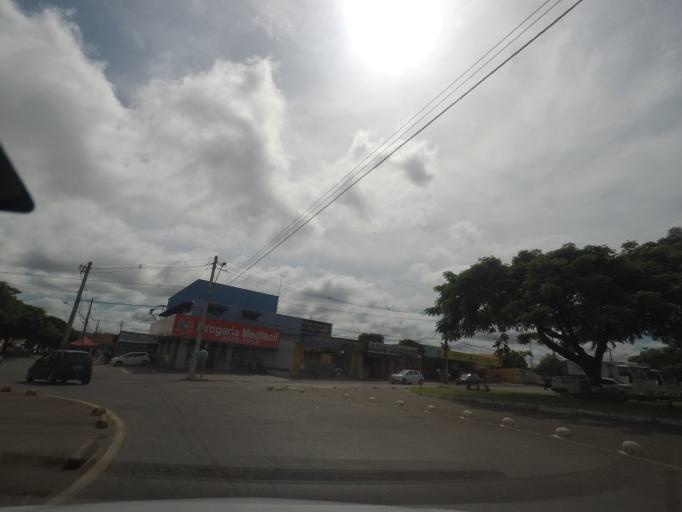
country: BR
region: Goias
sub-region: Goiania
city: Goiania
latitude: -16.6643
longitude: -49.2146
